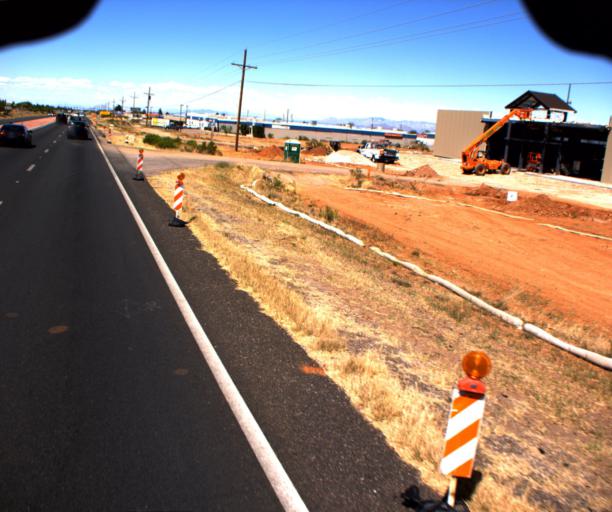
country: US
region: Arizona
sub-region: Cochise County
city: Sierra Vista Southeast
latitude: 31.4975
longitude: -110.2573
